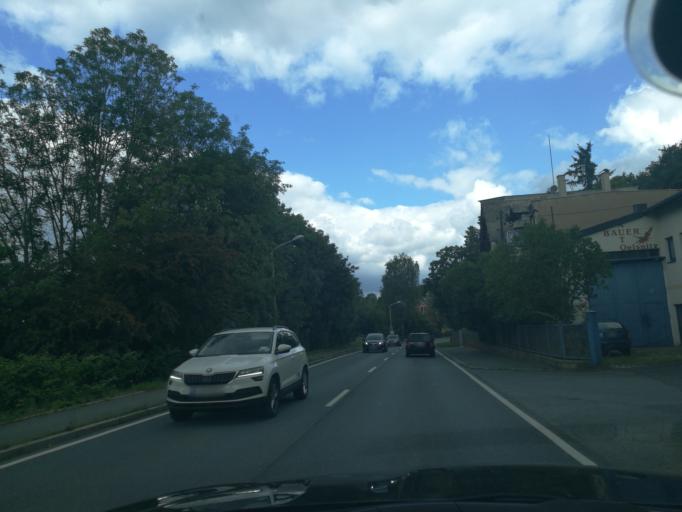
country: DE
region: Saxony
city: Oelsnitz
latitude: 50.4081
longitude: 12.1806
